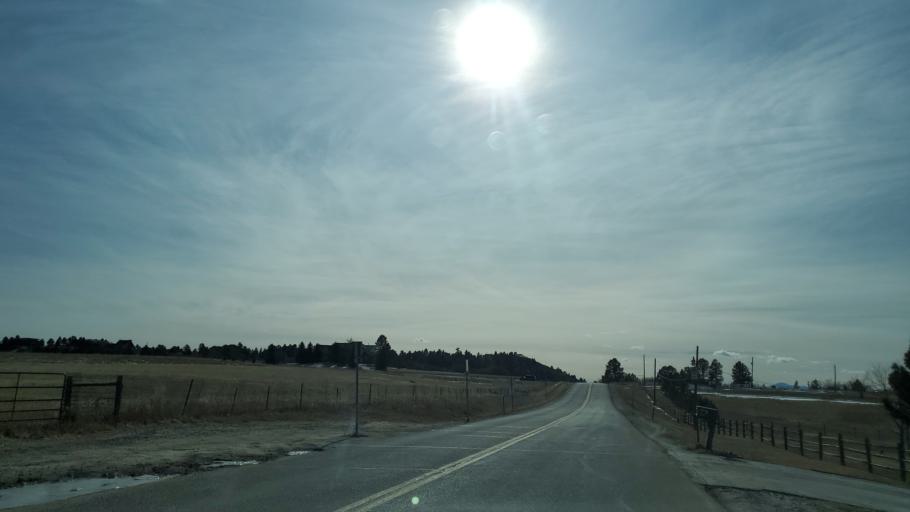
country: US
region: Colorado
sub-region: Douglas County
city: Castle Pines
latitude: 39.4497
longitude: -104.8726
